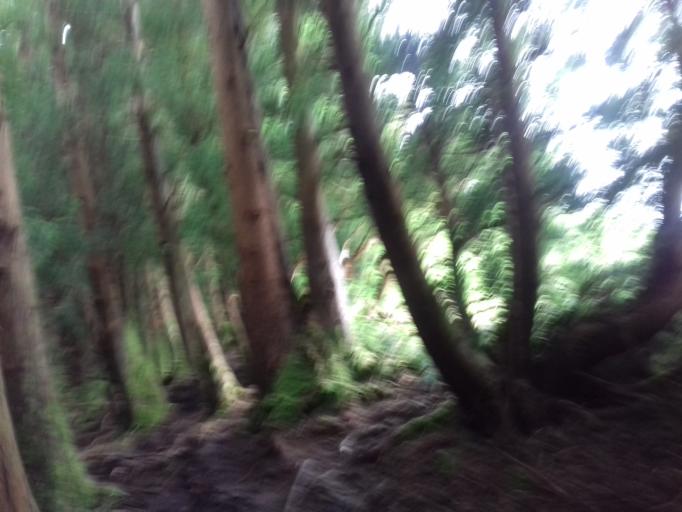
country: PT
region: Azores
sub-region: Praia da Vitoria
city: Biscoitos
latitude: 38.7297
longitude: -27.2815
